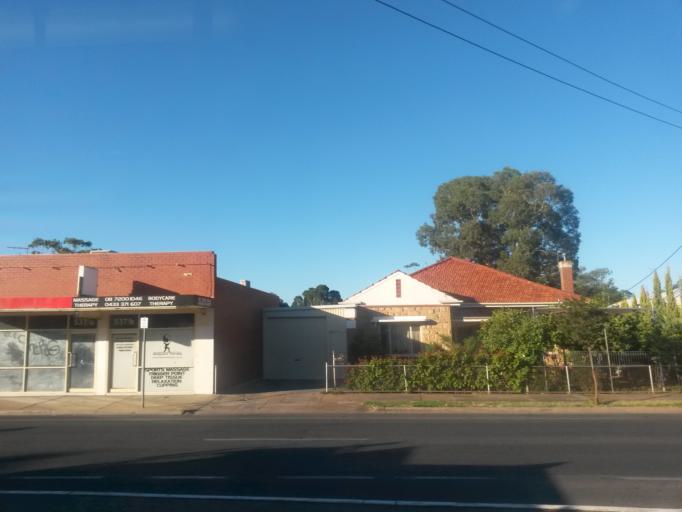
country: AU
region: South Australia
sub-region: Charles Sturt
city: Woodville North
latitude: -34.8717
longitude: 138.5426
